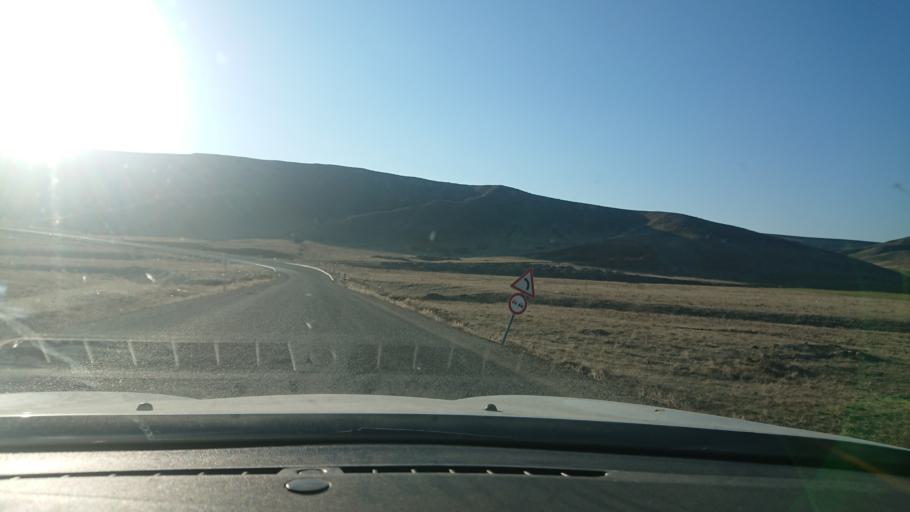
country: TR
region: Aksaray
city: Acipinar
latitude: 38.7116
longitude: 33.7621
